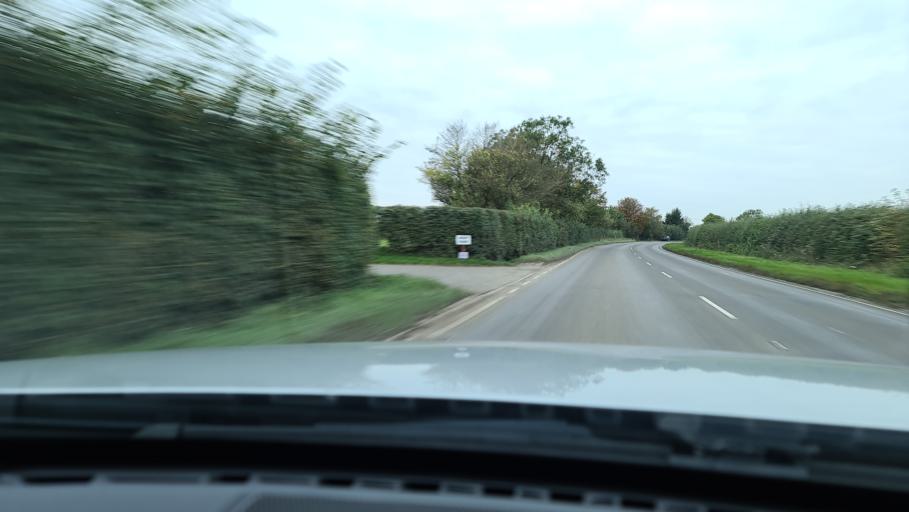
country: GB
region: England
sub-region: Buckinghamshire
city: Waddesdon
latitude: 51.8579
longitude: -0.9823
